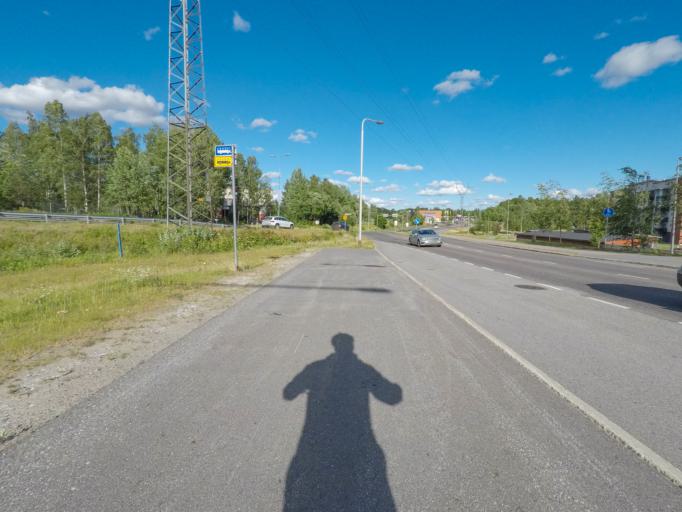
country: FI
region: South Karelia
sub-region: Lappeenranta
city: Lappeenranta
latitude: 61.0649
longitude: 28.1649
